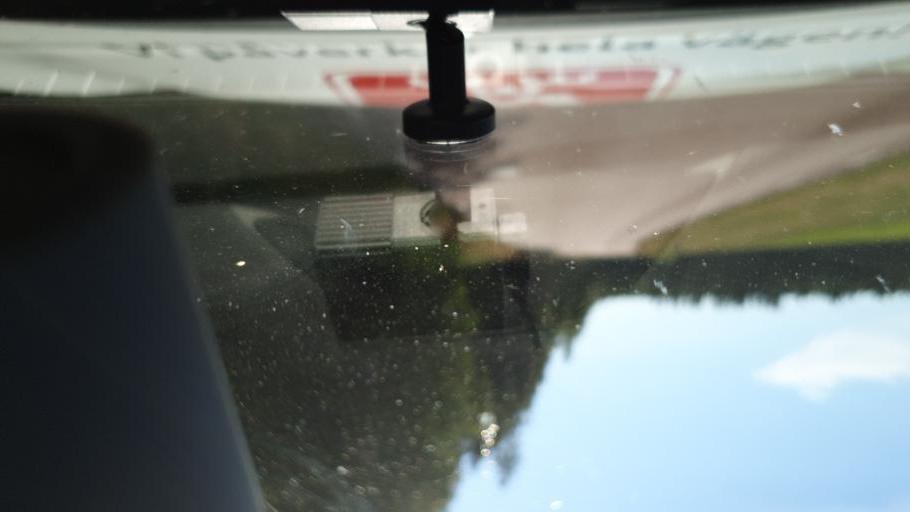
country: SE
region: Vaermland
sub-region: Kils Kommun
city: Kil
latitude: 59.4853
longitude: 13.2624
